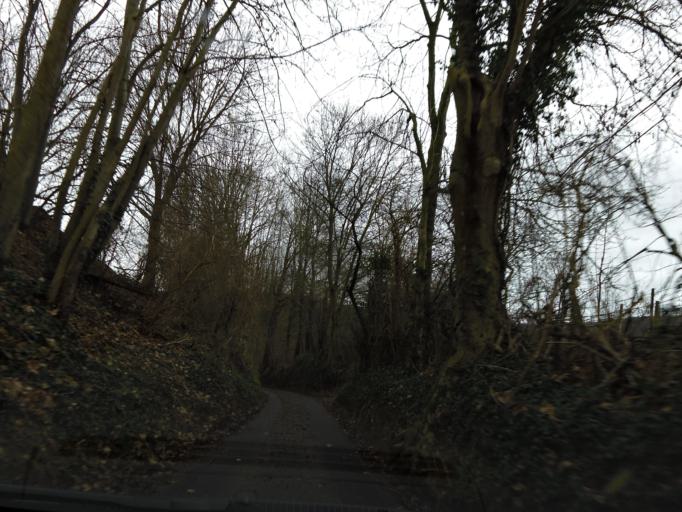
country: BE
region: Flanders
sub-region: Provincie Limburg
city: Sint-Pieters-Voeren
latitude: 50.7674
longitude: 5.8589
